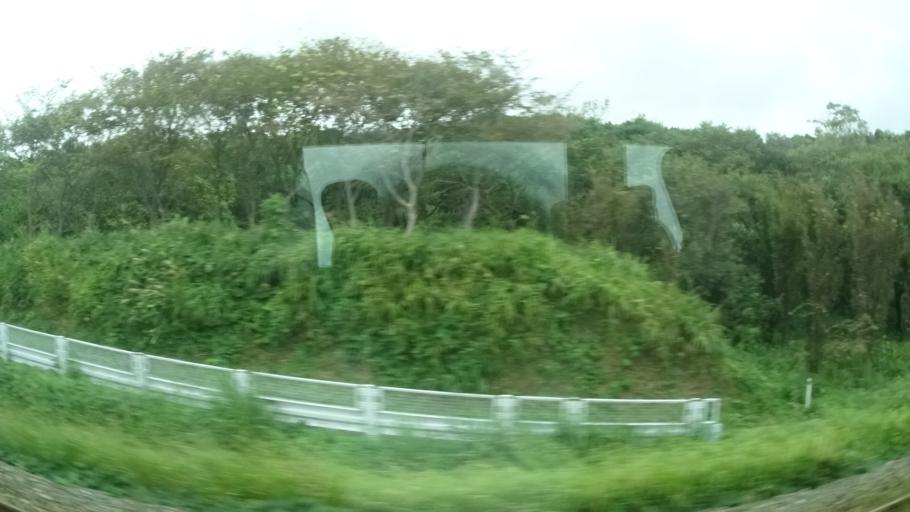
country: JP
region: Niigata
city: Murakami
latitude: 38.5233
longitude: 139.5391
